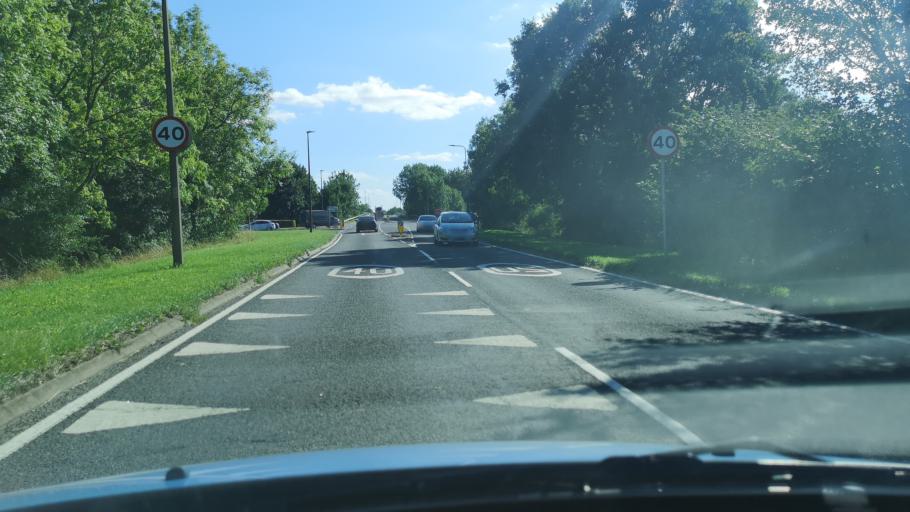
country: GB
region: England
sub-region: North Lincolnshire
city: Crowle
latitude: 53.5928
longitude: -0.8189
